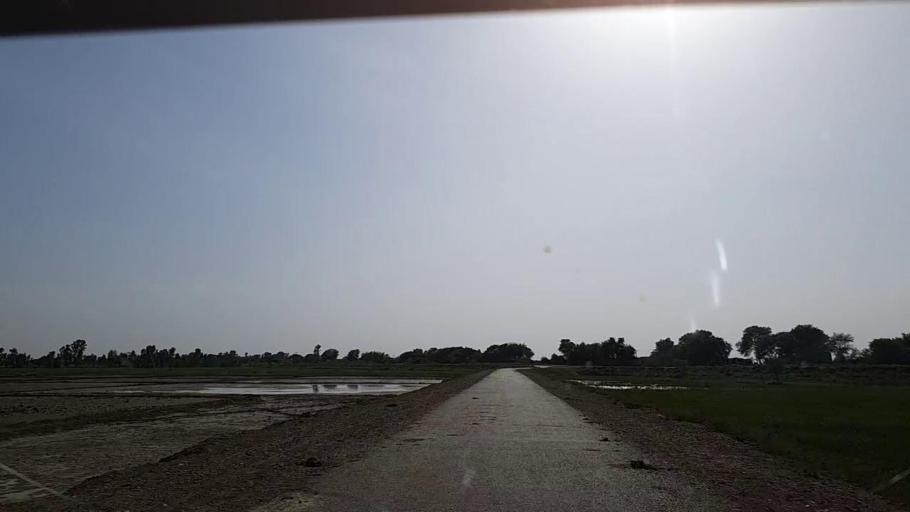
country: PK
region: Sindh
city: Phulji
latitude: 26.9903
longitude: 67.6477
